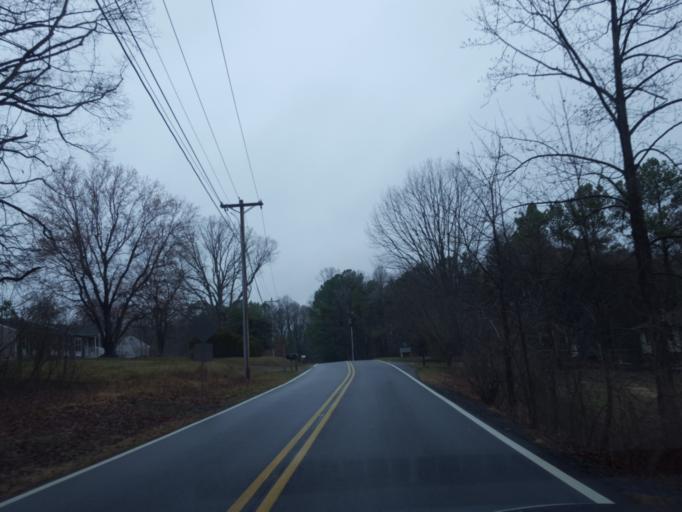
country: US
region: Maryland
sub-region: Calvert County
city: Huntingtown
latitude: 38.6108
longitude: -76.5481
